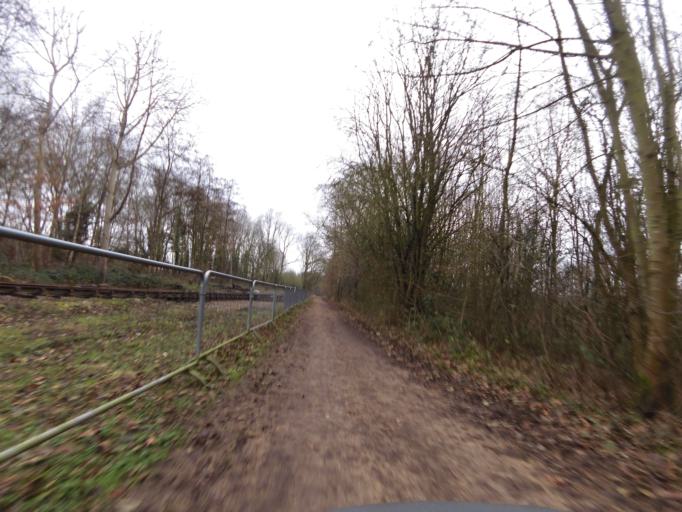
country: GB
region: England
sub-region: Norfolk
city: Briston
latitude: 52.7505
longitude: 1.0970
